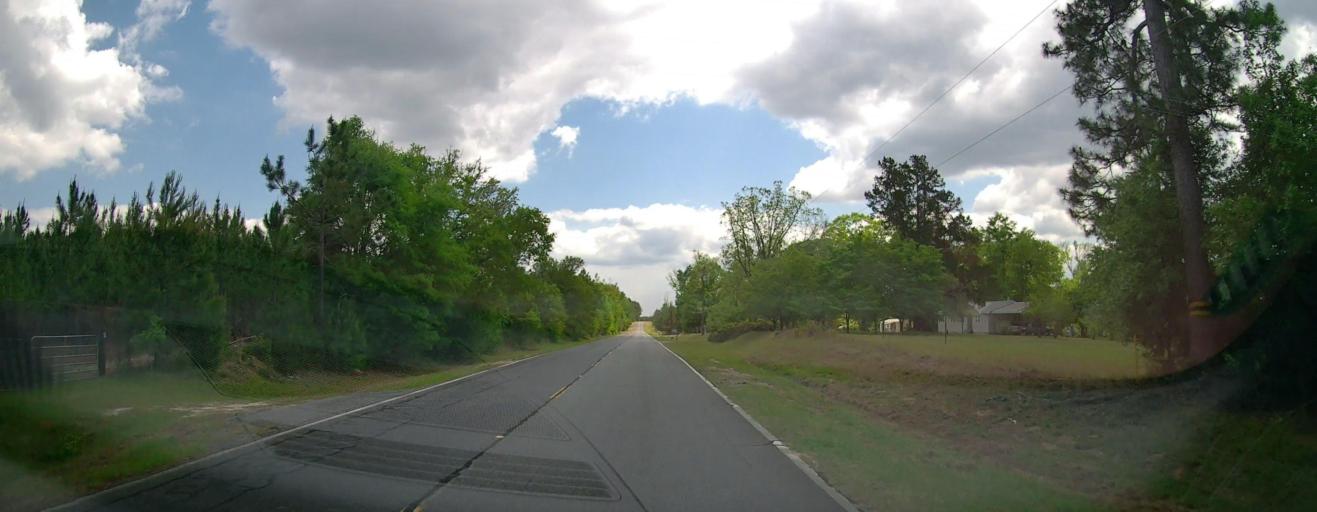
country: US
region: Georgia
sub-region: Treutlen County
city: Soperton
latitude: 32.4921
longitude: -82.6069
